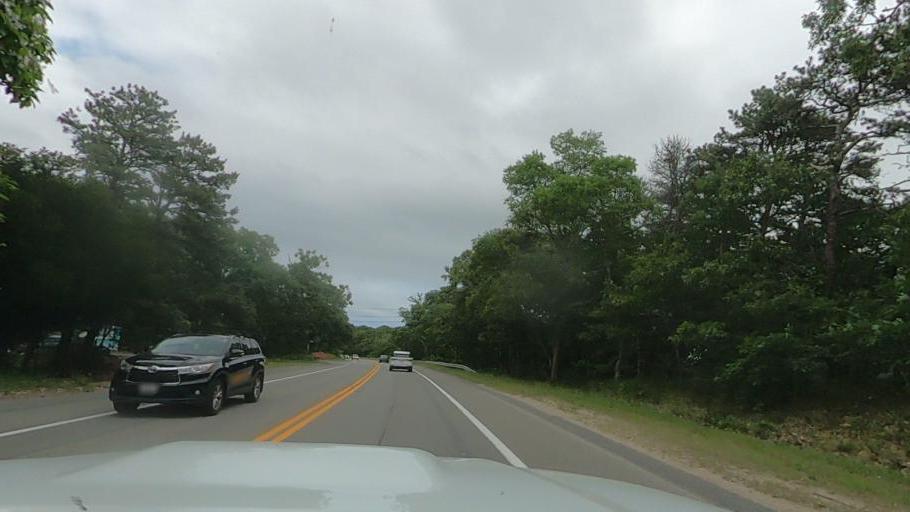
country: US
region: Massachusetts
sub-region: Barnstable County
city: Wellfleet
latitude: 41.9187
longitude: -70.0039
